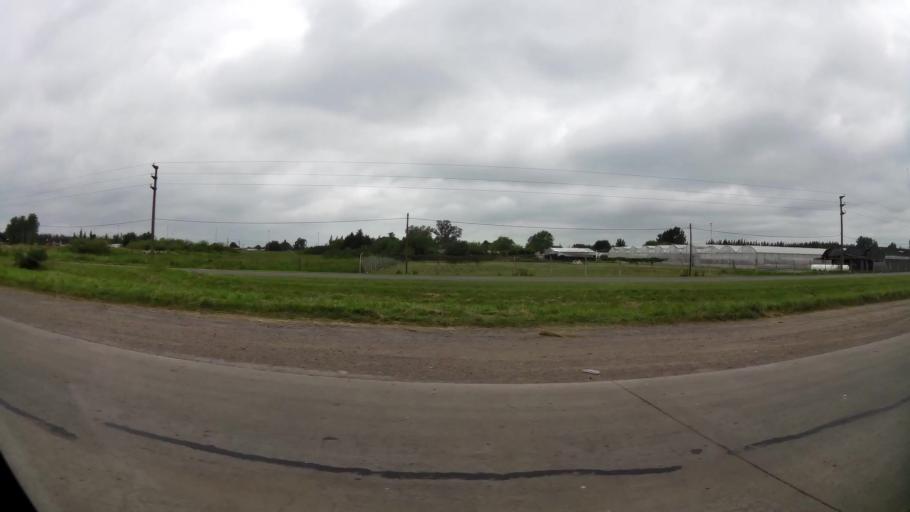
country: AR
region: Buenos Aires
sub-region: Partido de La Plata
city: La Plata
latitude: -35.0380
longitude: -58.0952
